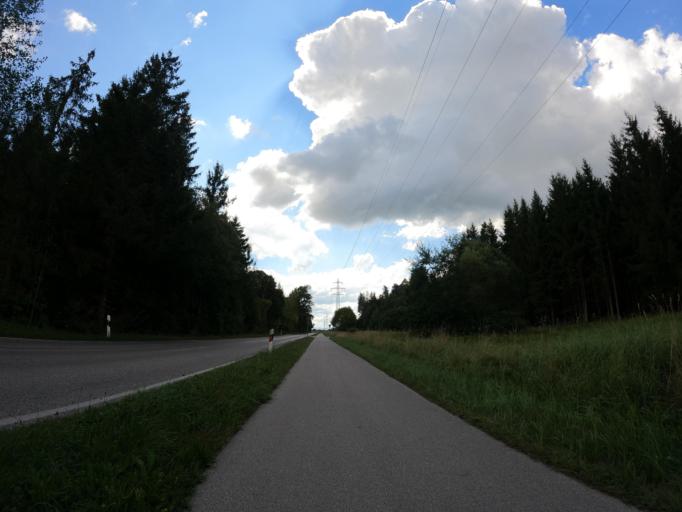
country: DE
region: Bavaria
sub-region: Upper Bavaria
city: Brunnthal
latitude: 48.0204
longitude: 11.6822
